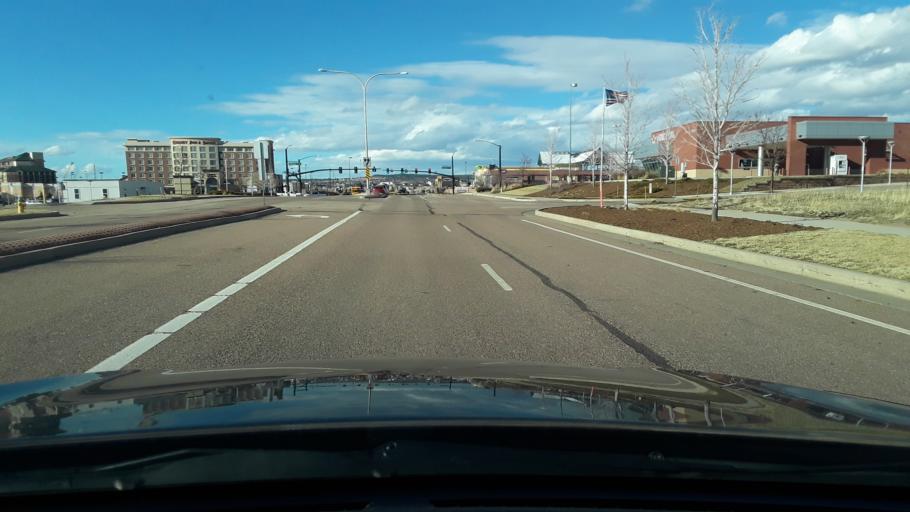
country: US
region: Colorado
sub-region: El Paso County
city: Air Force Academy
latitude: 38.9893
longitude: -104.8077
